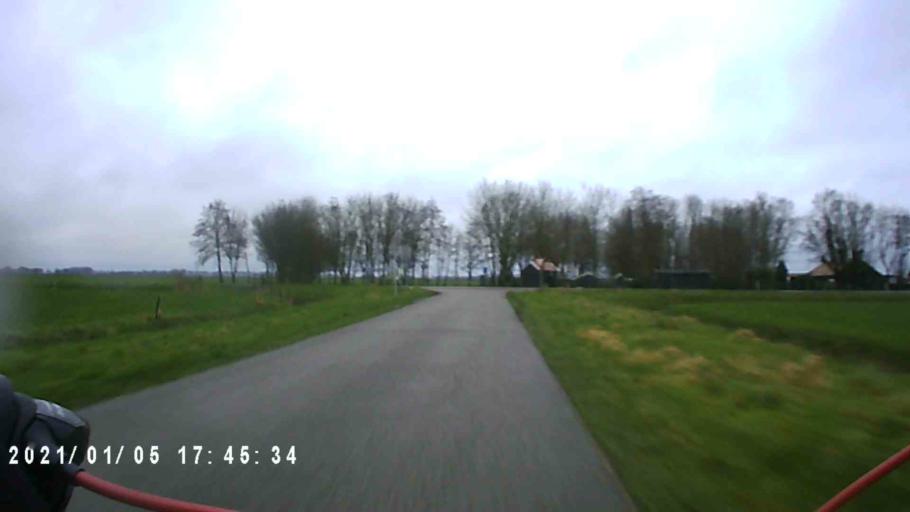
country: NL
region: Groningen
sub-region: Gemeente Veendam
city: Veendam
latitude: 53.2080
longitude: 6.9125
